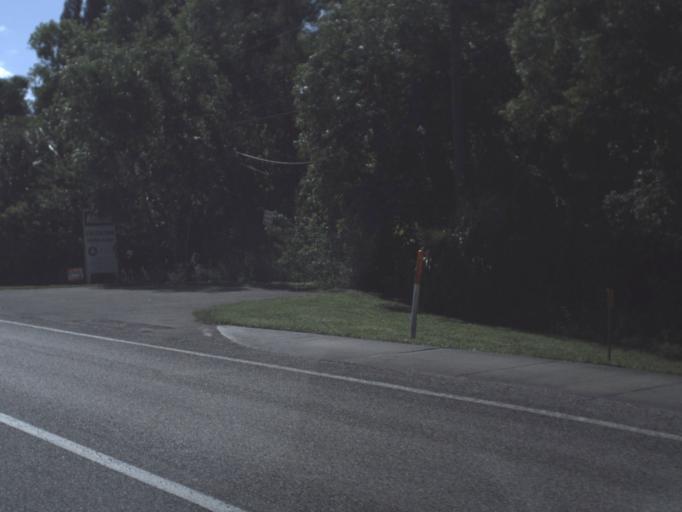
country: US
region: Florida
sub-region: Collier County
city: Lely Resort
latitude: 26.0666
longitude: -81.7046
